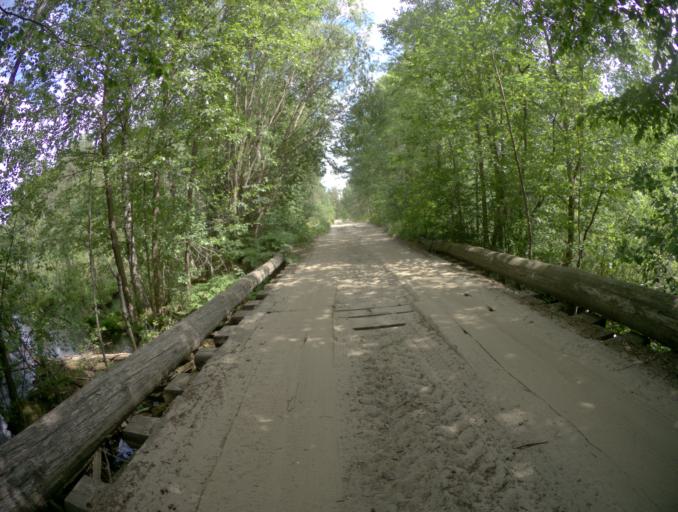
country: RU
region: Nizjnij Novgorod
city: Frolishchi
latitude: 56.4330
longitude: 42.6297
